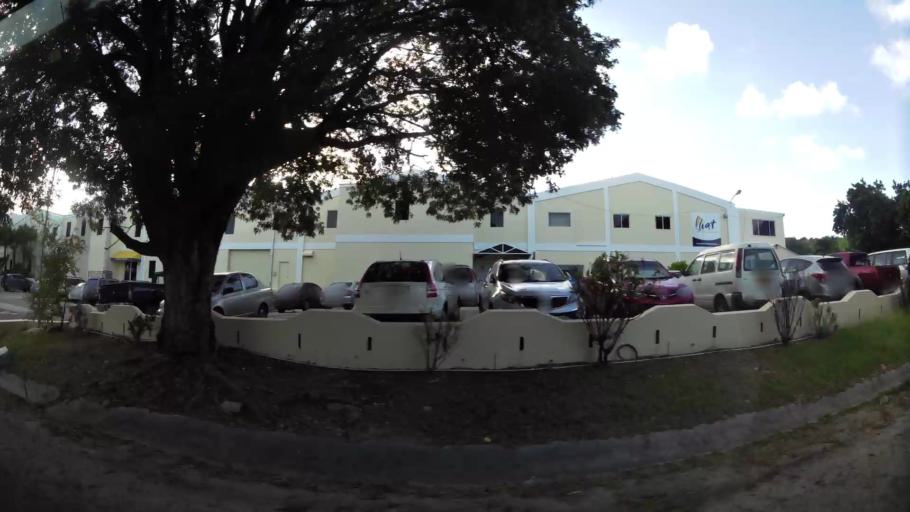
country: AG
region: Saint George
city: Piggotts
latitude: 17.1370
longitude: -61.7975
